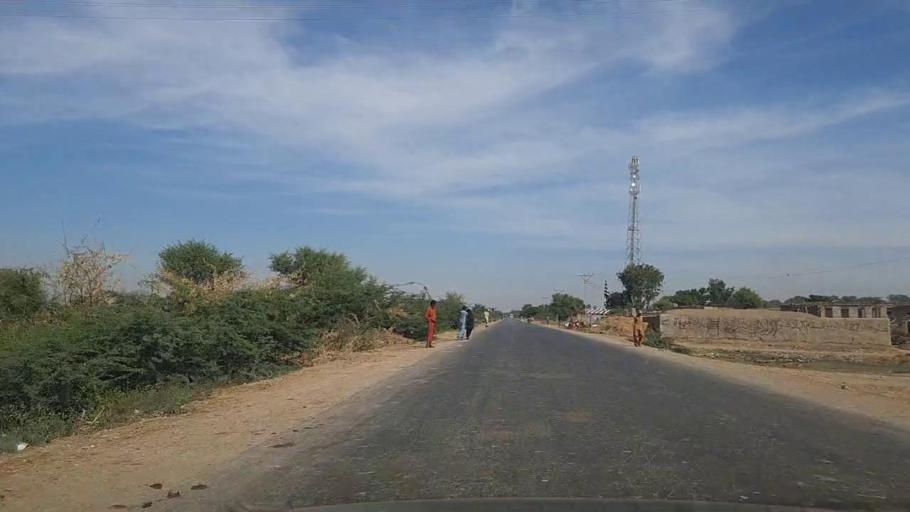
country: PK
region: Sindh
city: Daro Mehar
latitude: 24.9680
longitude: 68.1216
